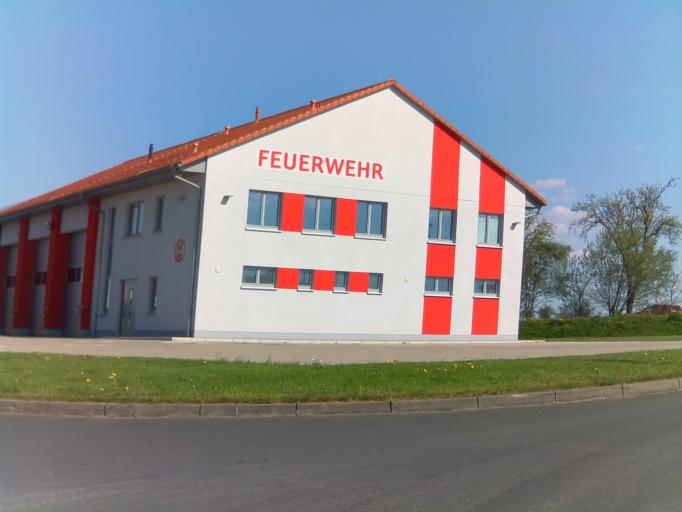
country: DE
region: Thuringia
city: Auma
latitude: 50.6943
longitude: 11.9038
